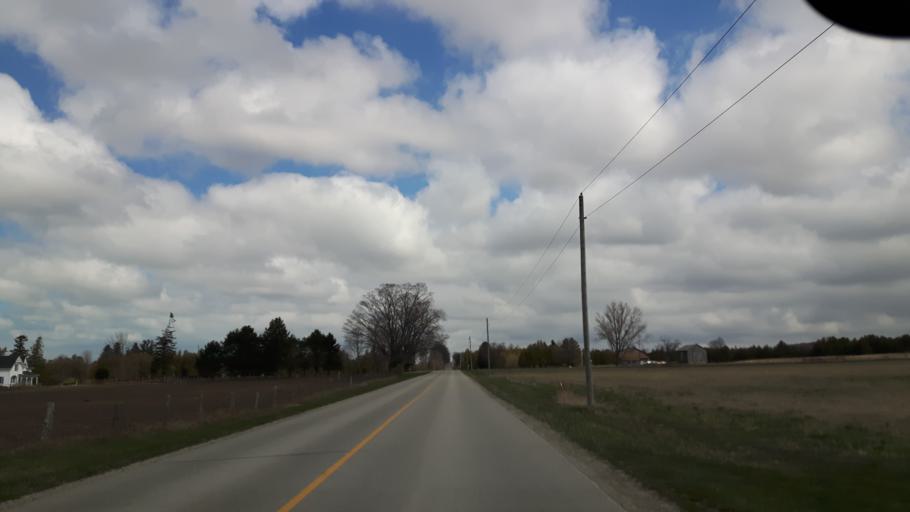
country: CA
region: Ontario
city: Goderich
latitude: 43.6632
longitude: -81.6846
